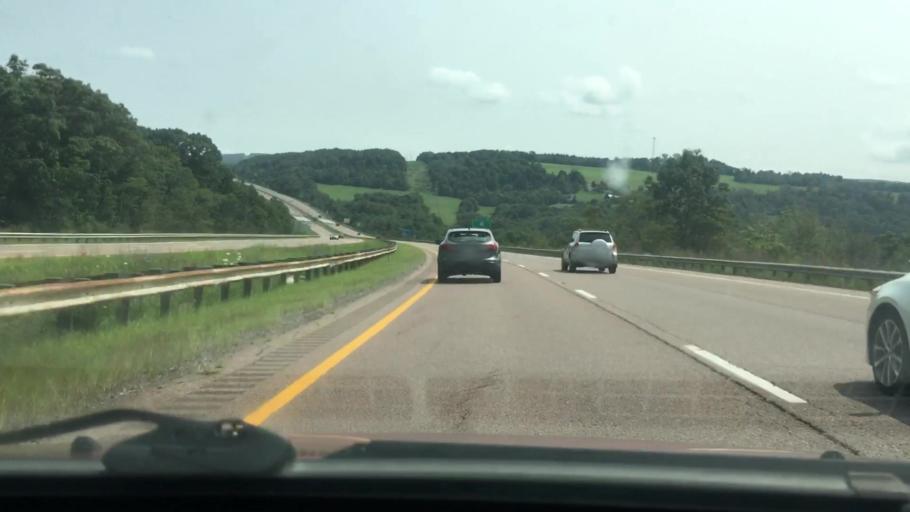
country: US
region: Maryland
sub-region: Allegany County
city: Frostburg
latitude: 39.6351
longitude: -78.9428
